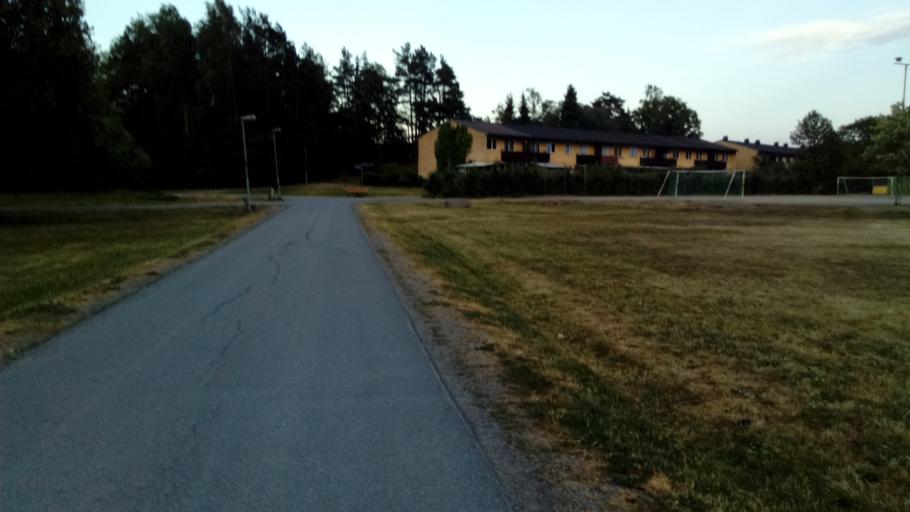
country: SE
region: Stockholm
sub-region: Tyreso Kommun
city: Bollmora
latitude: 59.2442
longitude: 18.2413
